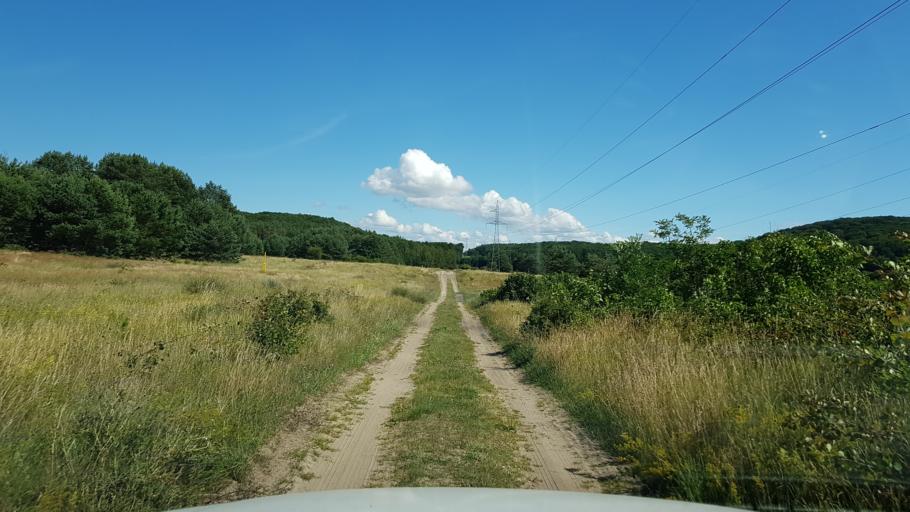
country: PL
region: West Pomeranian Voivodeship
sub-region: Powiat kamienski
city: Miedzyzdroje
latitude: 53.8846
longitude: 14.4437
